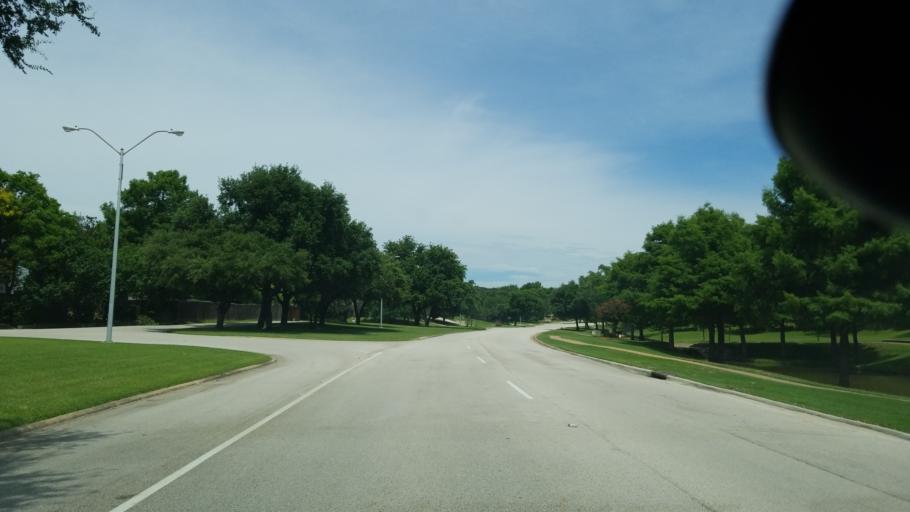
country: US
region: Texas
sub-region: Dallas County
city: Irving
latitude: 32.8473
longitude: -96.9376
